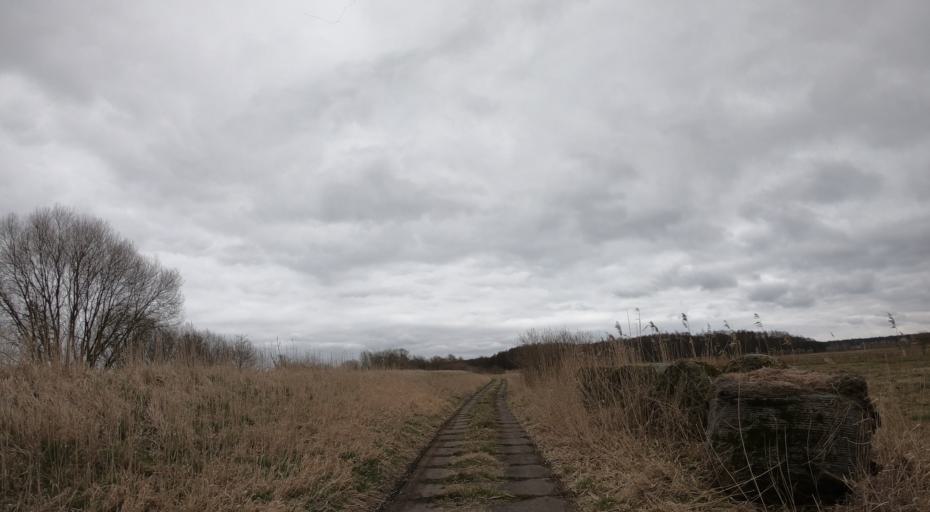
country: PL
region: West Pomeranian Voivodeship
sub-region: Powiat policki
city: Nowe Warpno
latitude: 53.6860
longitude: 14.3900
